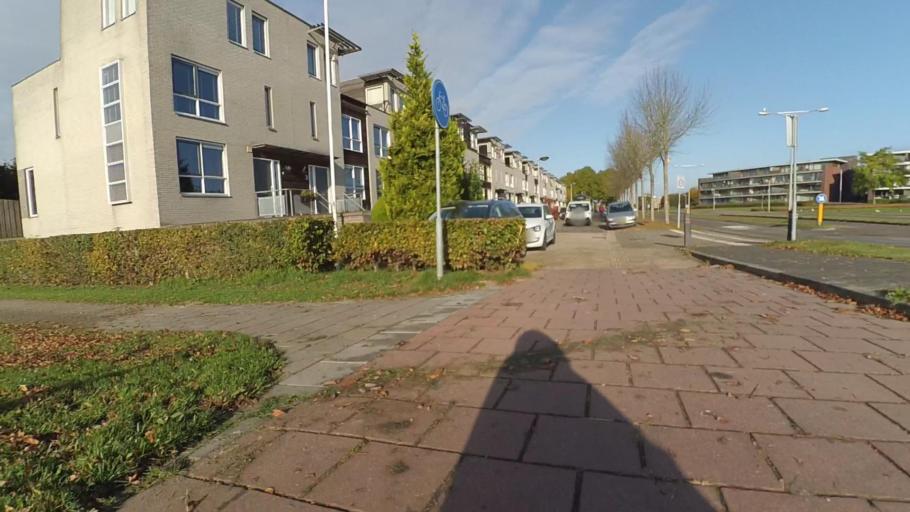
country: NL
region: Flevoland
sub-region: Gemeente Zeewolde
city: Zeewolde
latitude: 52.3341
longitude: 5.5183
